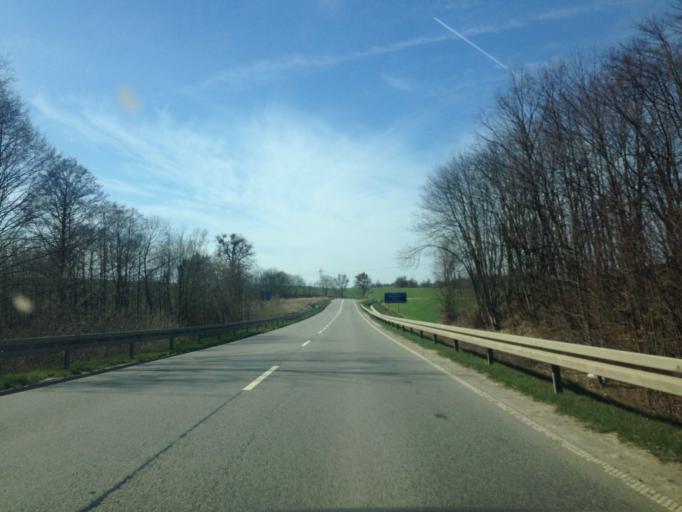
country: PL
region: Pomeranian Voivodeship
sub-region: Powiat starogardzki
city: Smetowo Graniczne
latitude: 53.7349
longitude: 18.7189
